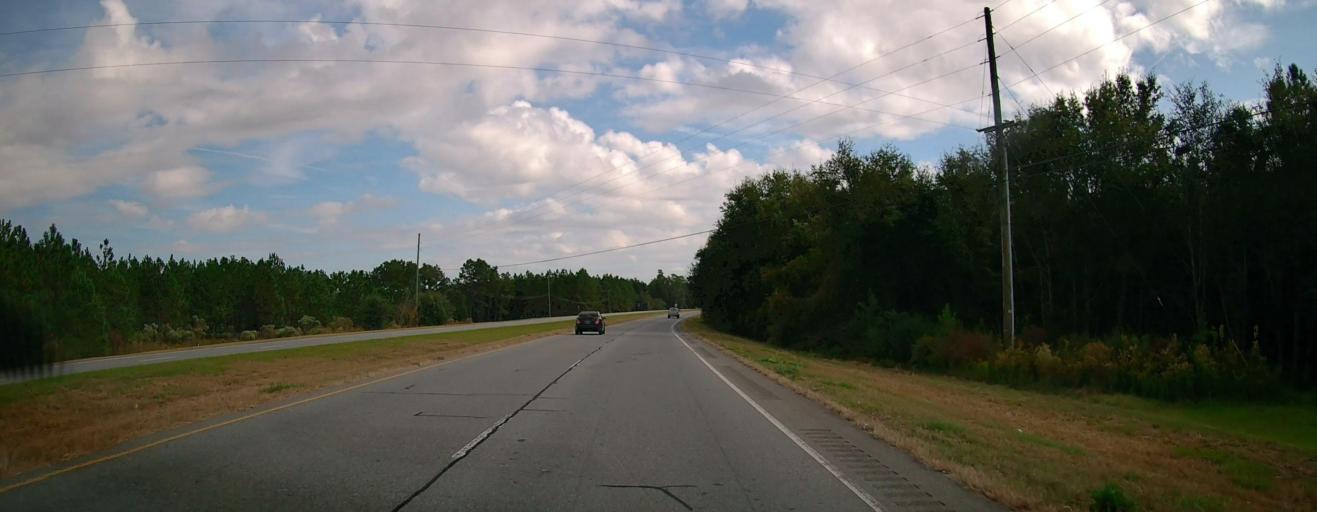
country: US
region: Georgia
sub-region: Mitchell County
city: Camilla
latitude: 31.2167
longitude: -84.1845
